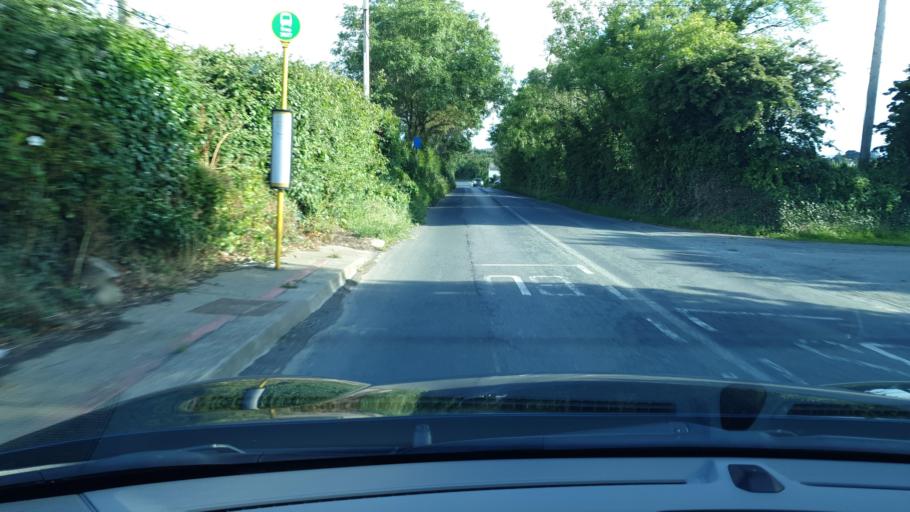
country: IE
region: Leinster
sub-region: Fingal County
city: Skerries
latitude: 53.5542
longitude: -6.1018
